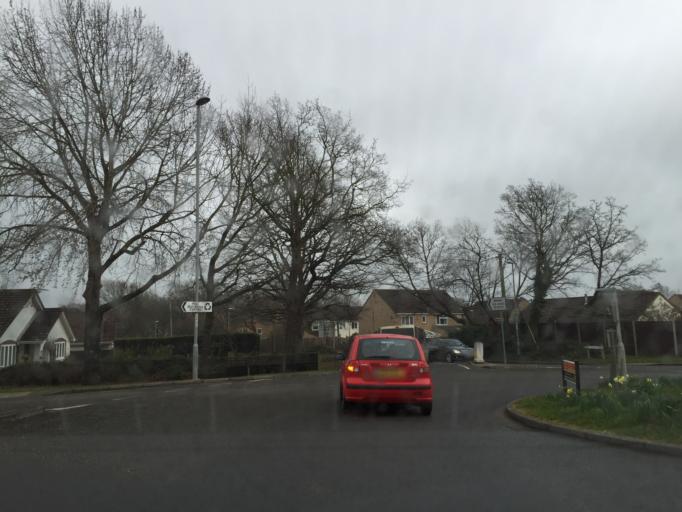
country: GB
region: England
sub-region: Dorset
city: Verwood
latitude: 50.8745
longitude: -1.8767
